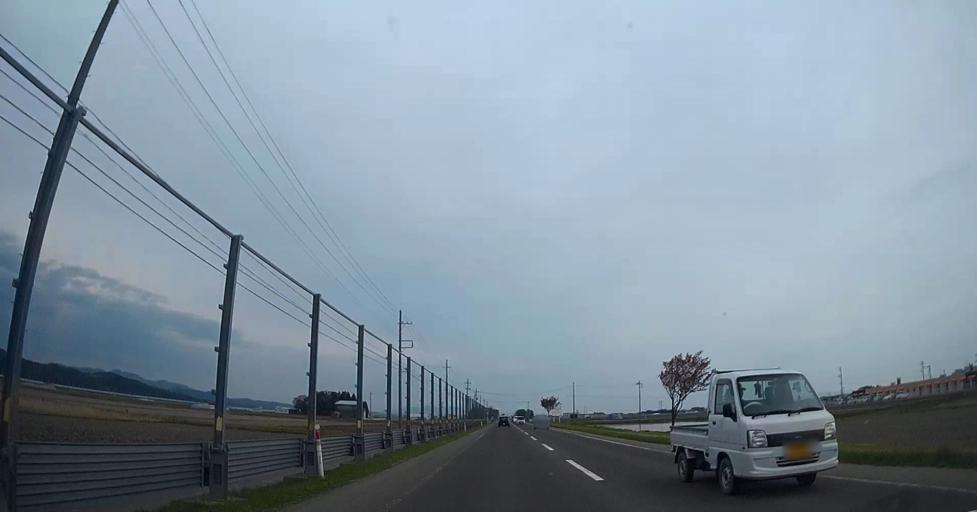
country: JP
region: Aomori
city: Aomori Shi
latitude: 40.8886
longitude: 140.6693
